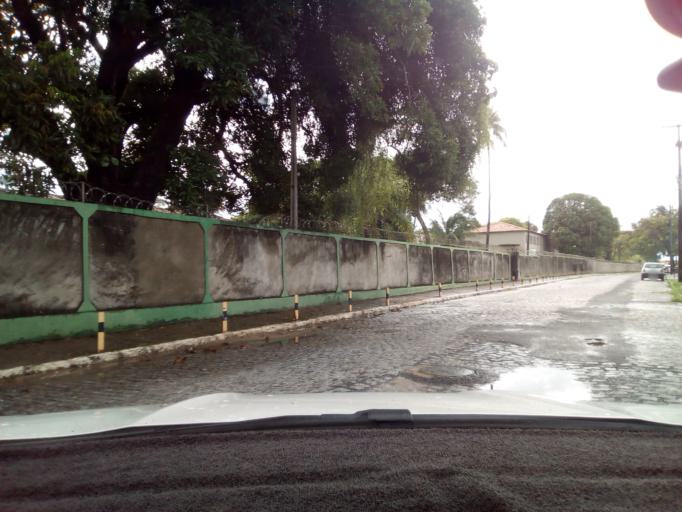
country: BR
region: Paraiba
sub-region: Joao Pessoa
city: Joao Pessoa
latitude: -7.1384
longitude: -34.8830
